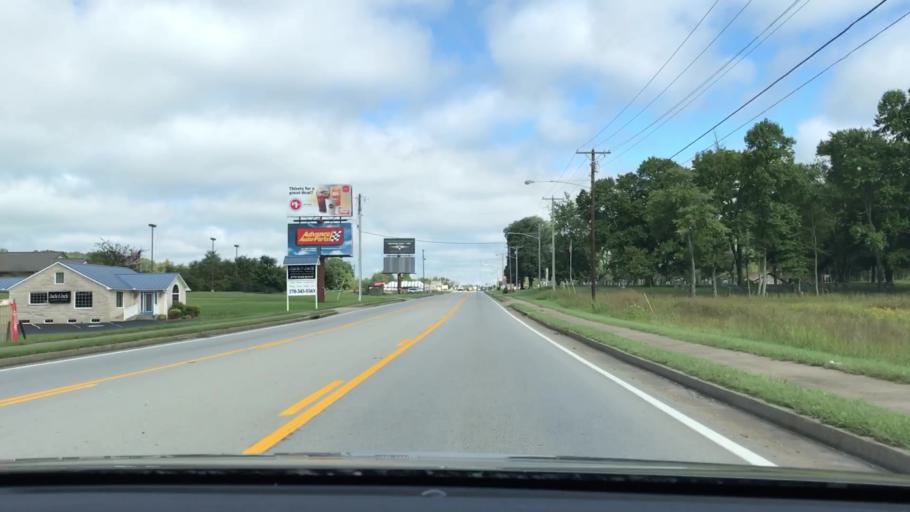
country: US
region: Kentucky
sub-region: Russell County
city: Jamestown
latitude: 37.0162
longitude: -85.0759
